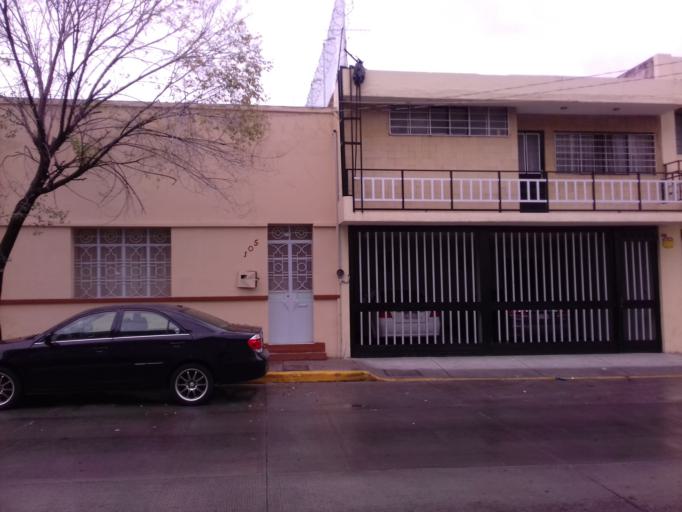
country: MX
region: Aguascalientes
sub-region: Aguascalientes
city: Aguascalientes
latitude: 21.8839
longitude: -102.2873
